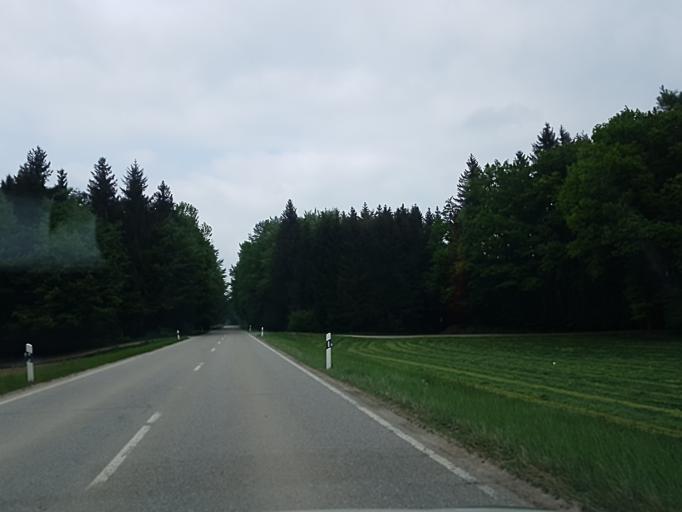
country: DE
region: Bavaria
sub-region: Upper Bavaria
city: Ebersberg
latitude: 48.1047
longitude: 11.9805
